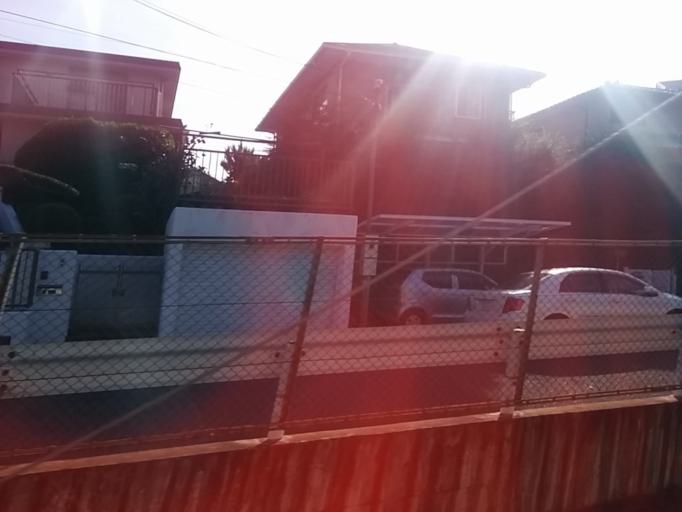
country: JP
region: Nara
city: Nara-shi
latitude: 34.7146
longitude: 135.7922
